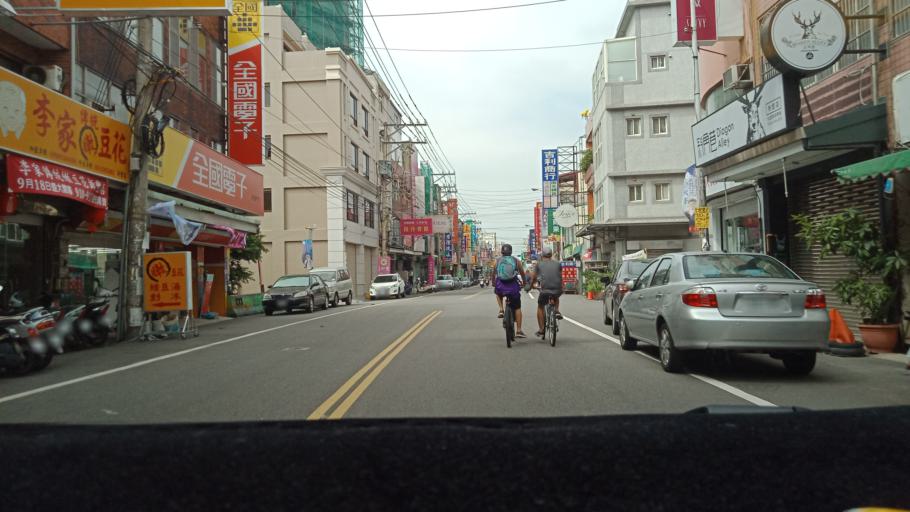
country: TW
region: Taiwan
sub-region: Hsinchu
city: Zhubei
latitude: 24.8715
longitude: 120.9953
